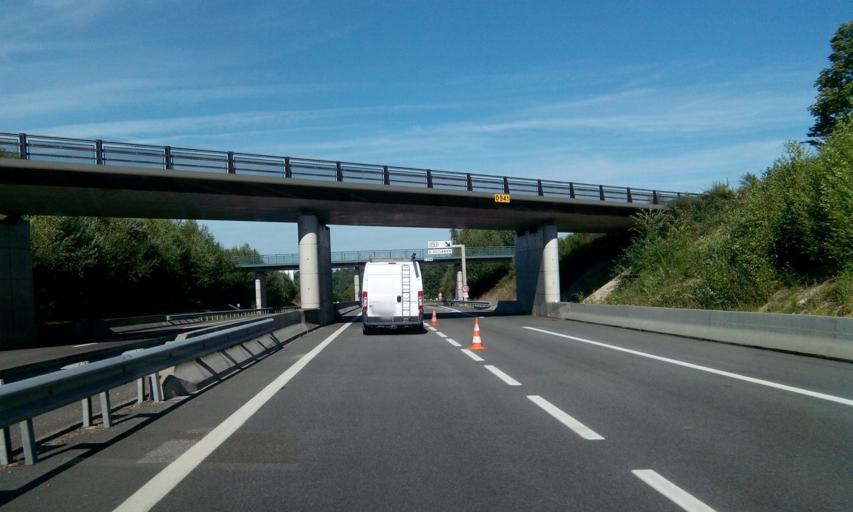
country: FR
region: Limousin
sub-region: Departement de la Haute-Vienne
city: Veyrac
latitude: 45.8888
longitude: 1.0628
